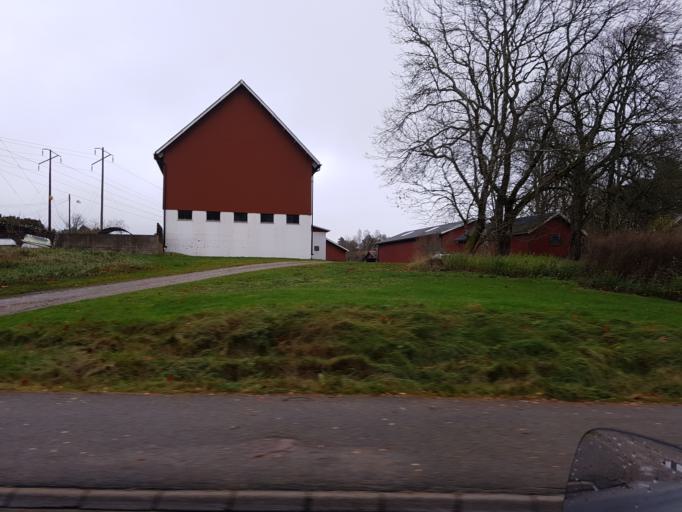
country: SE
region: Vaestra Goetaland
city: Svanesund
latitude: 58.1477
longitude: 11.8037
